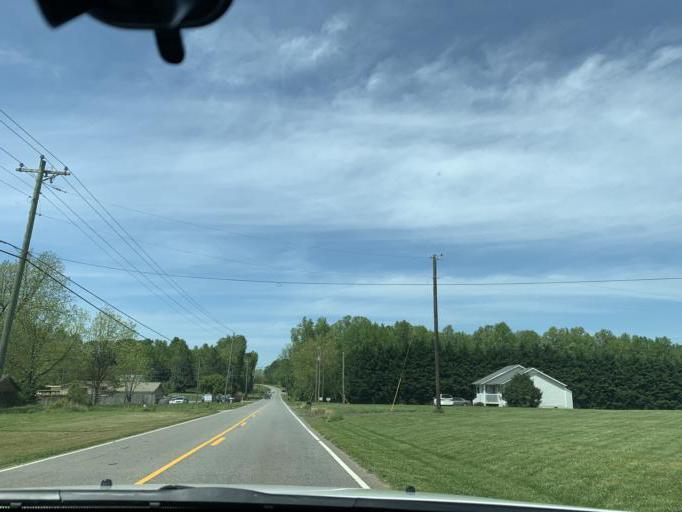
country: US
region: Georgia
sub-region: Forsyth County
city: Cumming
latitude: 34.2494
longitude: -84.1702
